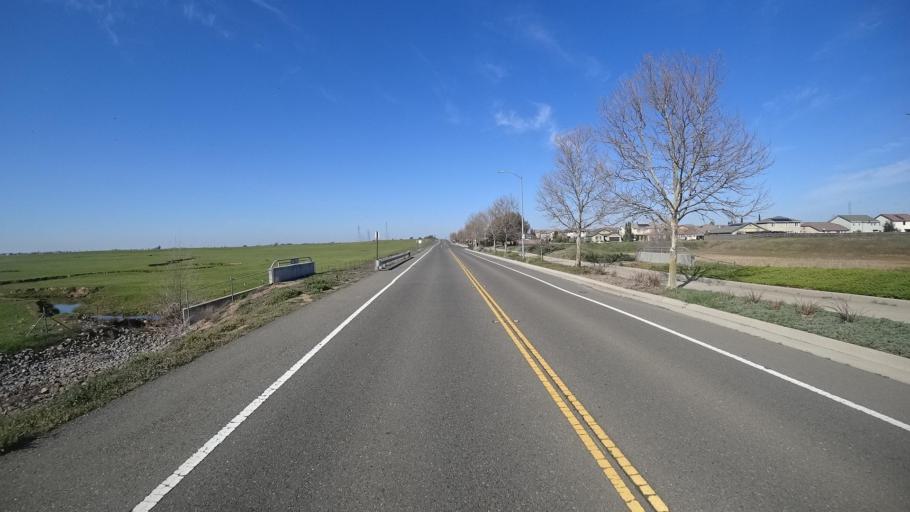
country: US
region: California
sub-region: Sacramento County
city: Rancho Cordova
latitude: 38.5253
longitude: -121.2303
